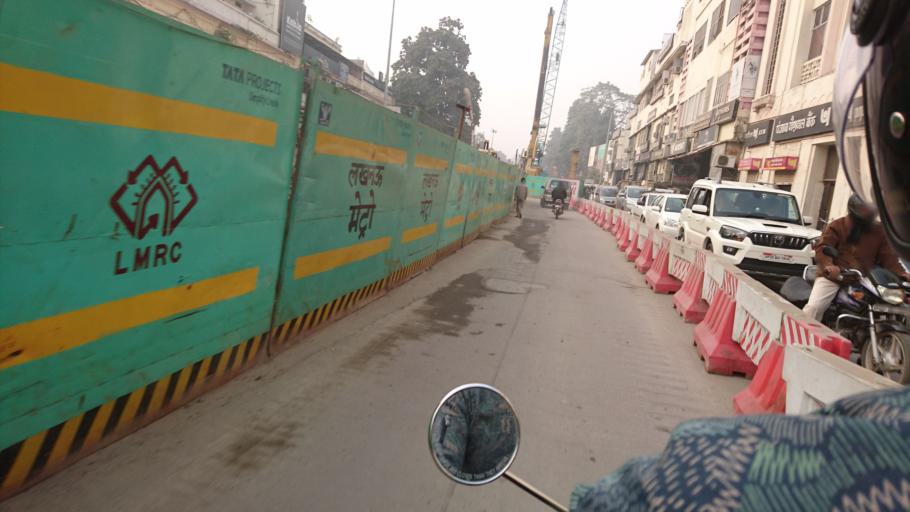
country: IN
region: Uttar Pradesh
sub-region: Lucknow District
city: Lucknow
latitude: 26.8499
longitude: 80.9417
